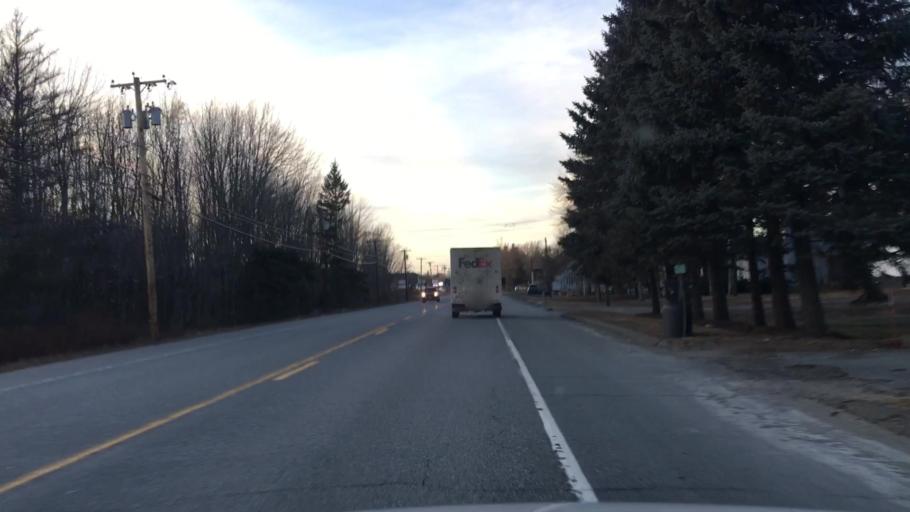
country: US
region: Maine
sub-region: Penobscot County
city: Holden
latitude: 44.7578
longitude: -68.6897
